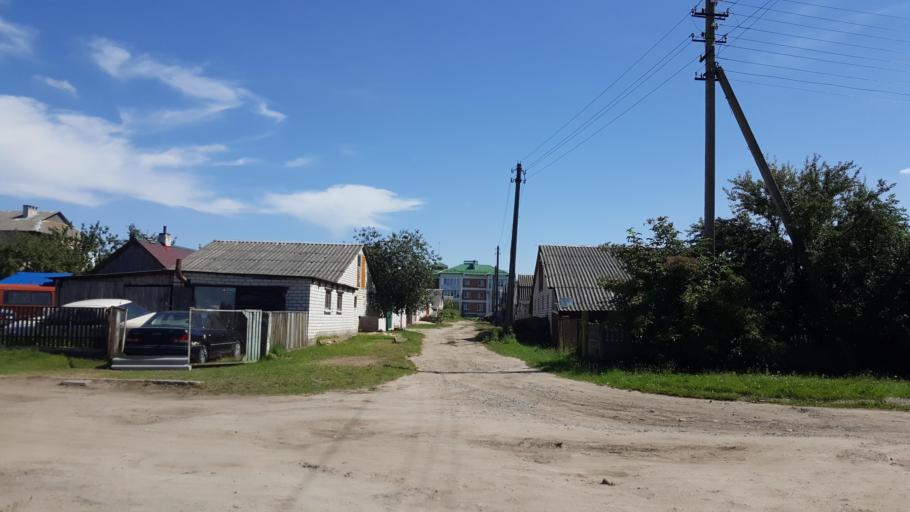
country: BY
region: Brest
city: Charnawchytsy
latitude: 52.2637
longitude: 23.5908
